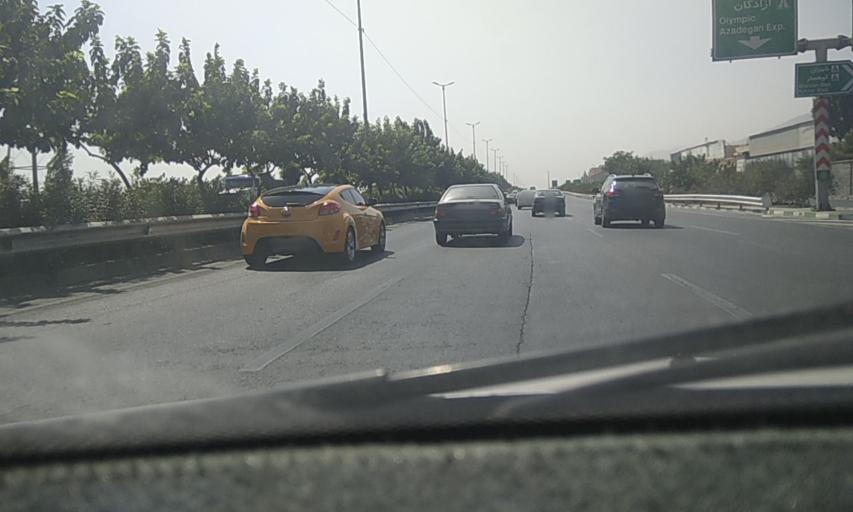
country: IR
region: Tehran
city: Tehran
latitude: 35.7533
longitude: 51.2992
